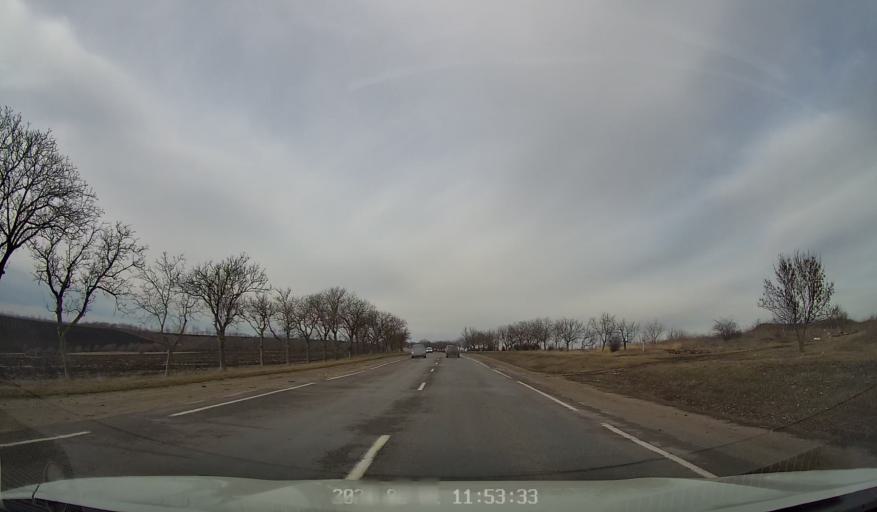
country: MD
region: Riscani
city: Riscani
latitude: 47.8756
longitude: 27.7197
